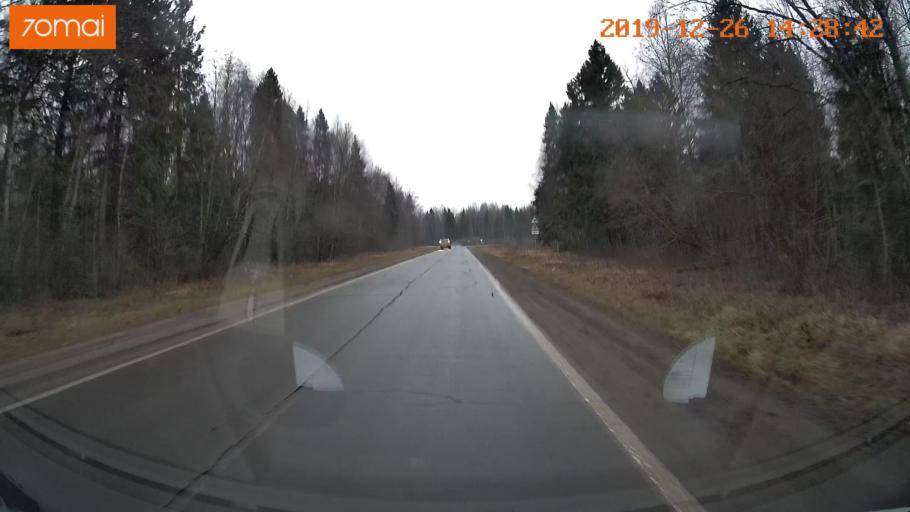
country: RU
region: Jaroslavl
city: Poshekhon'ye
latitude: 58.4729
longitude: 39.0501
